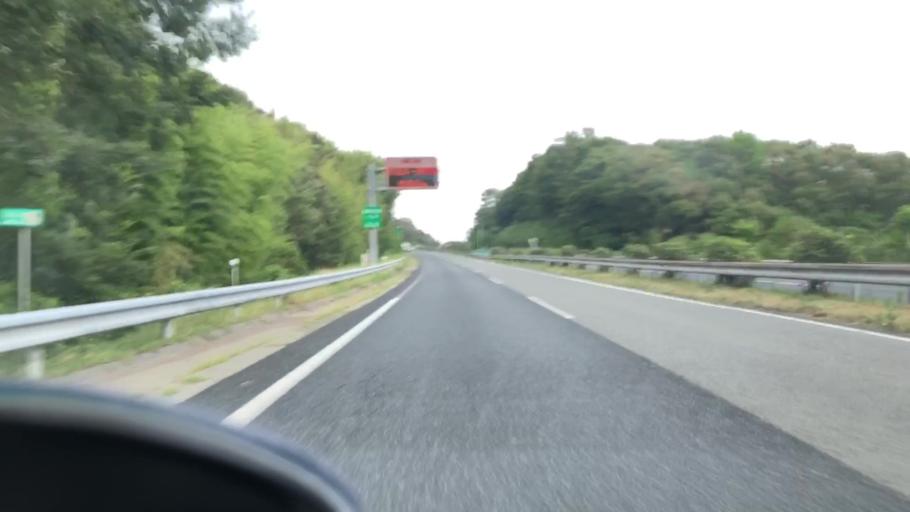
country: JP
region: Hyogo
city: Sandacho
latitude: 34.8868
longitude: 135.1111
